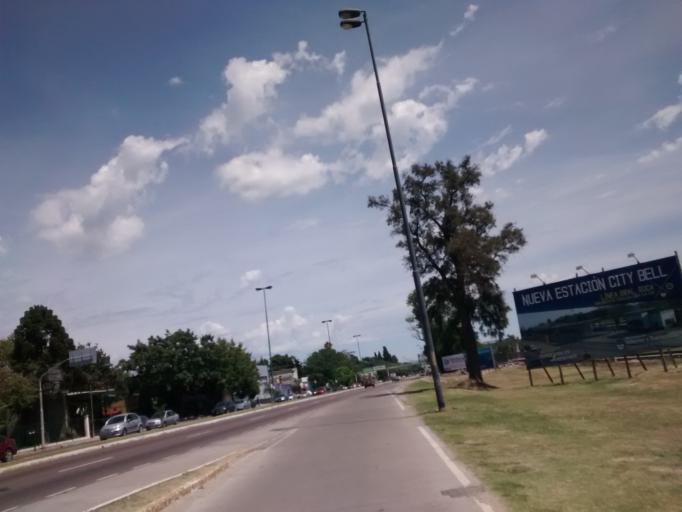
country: AR
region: Buenos Aires
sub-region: Partido de La Plata
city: La Plata
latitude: -34.8674
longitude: -58.0393
